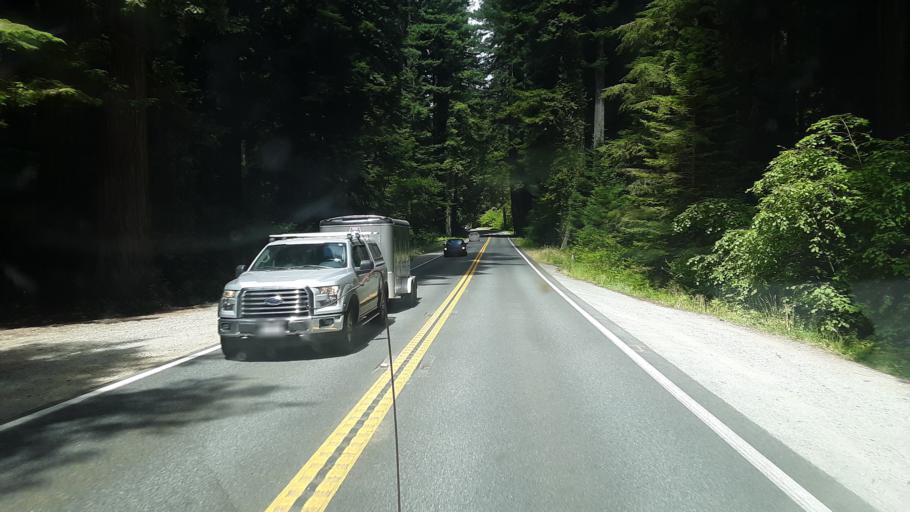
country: US
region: California
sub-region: Del Norte County
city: Bertsch-Oceanview
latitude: 41.8104
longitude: -124.0900
